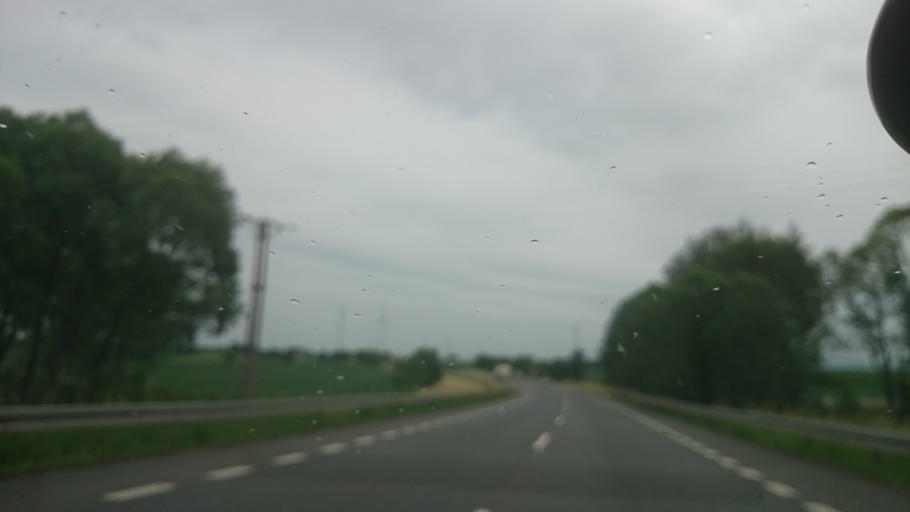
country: PL
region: Opole Voivodeship
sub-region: Powiat nyski
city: Paczkow
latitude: 50.4558
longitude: 16.9861
